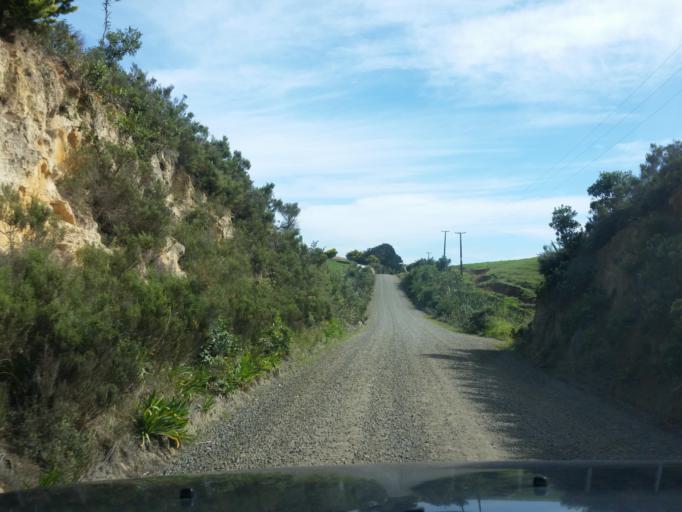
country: NZ
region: Northland
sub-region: Kaipara District
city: Dargaville
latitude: -35.9272
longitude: 173.7409
